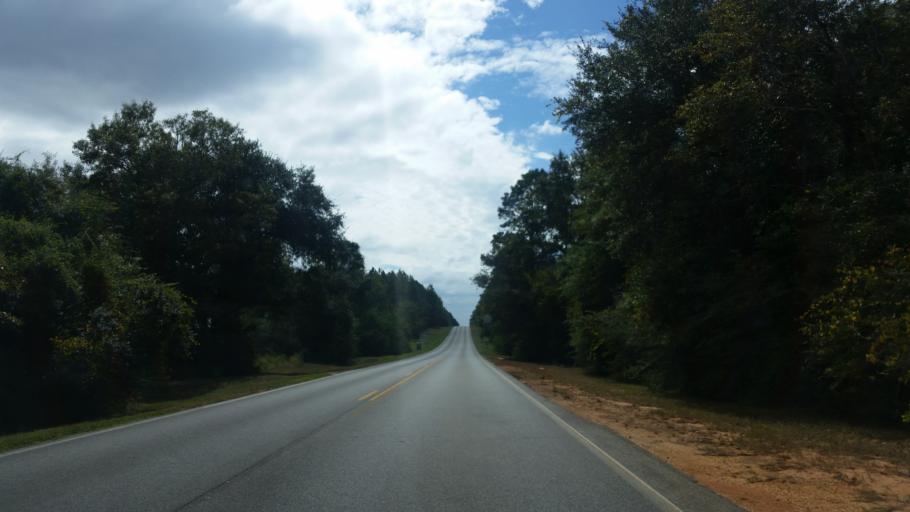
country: US
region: Florida
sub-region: Santa Rosa County
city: Point Baker
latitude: 30.7430
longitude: -86.9462
